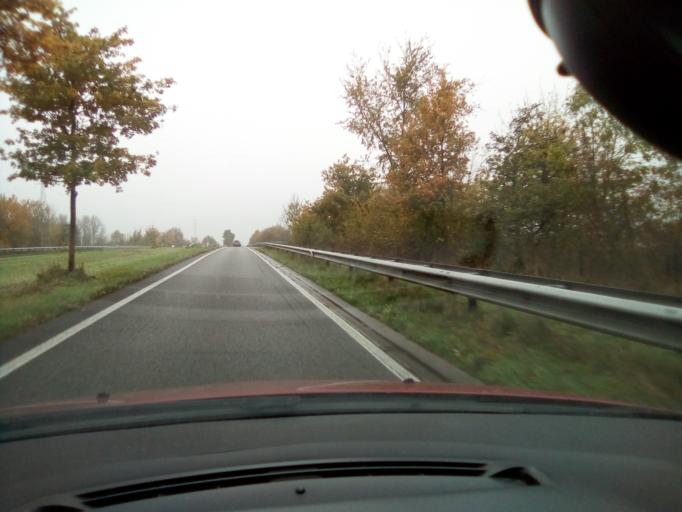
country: BE
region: Flanders
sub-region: Provincie Oost-Vlaanderen
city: Sint-Niklaas
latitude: 51.1479
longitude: 4.1247
